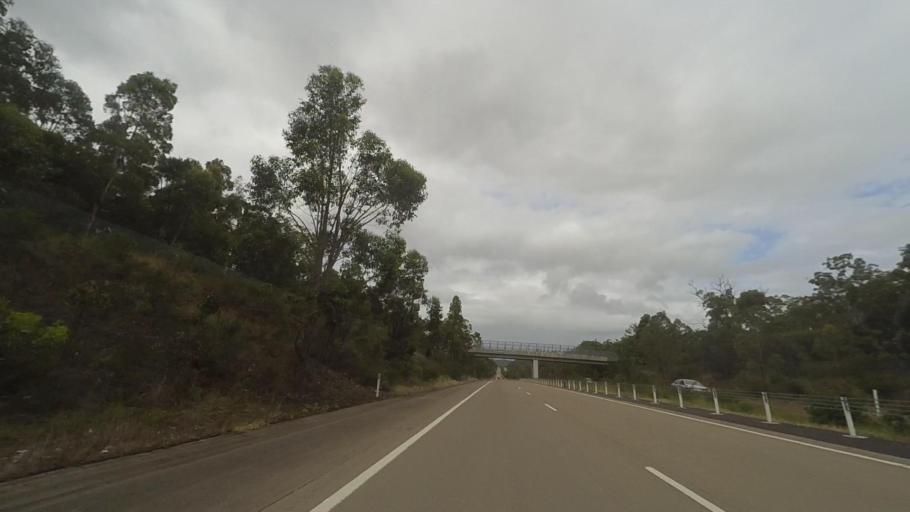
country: AU
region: New South Wales
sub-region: Port Stephens Shire
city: Medowie
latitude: -32.6412
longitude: 151.9298
